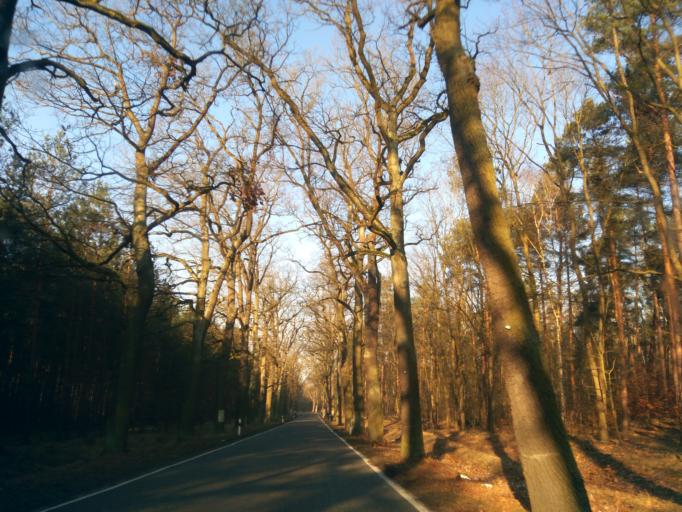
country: DE
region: Brandenburg
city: Falkensee
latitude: 52.6168
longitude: 13.1031
